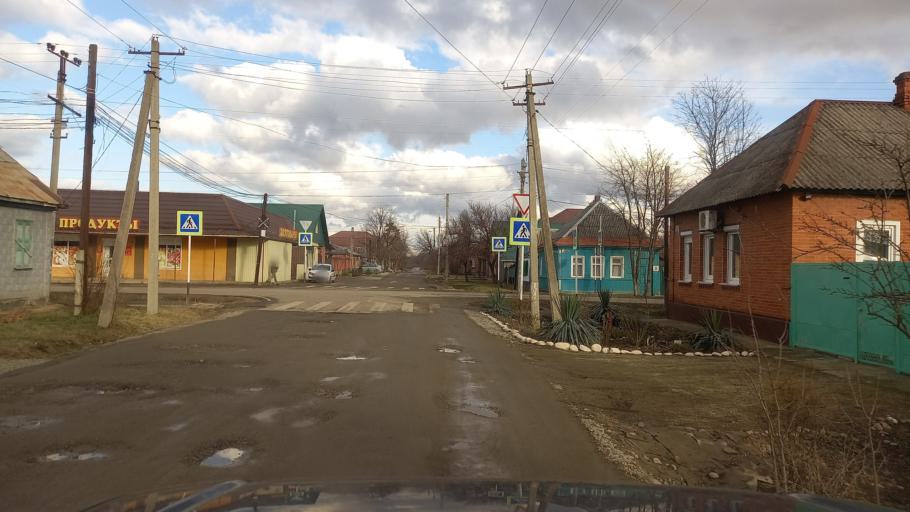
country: RU
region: Adygeya
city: Maykop
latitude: 44.5956
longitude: 40.0801
